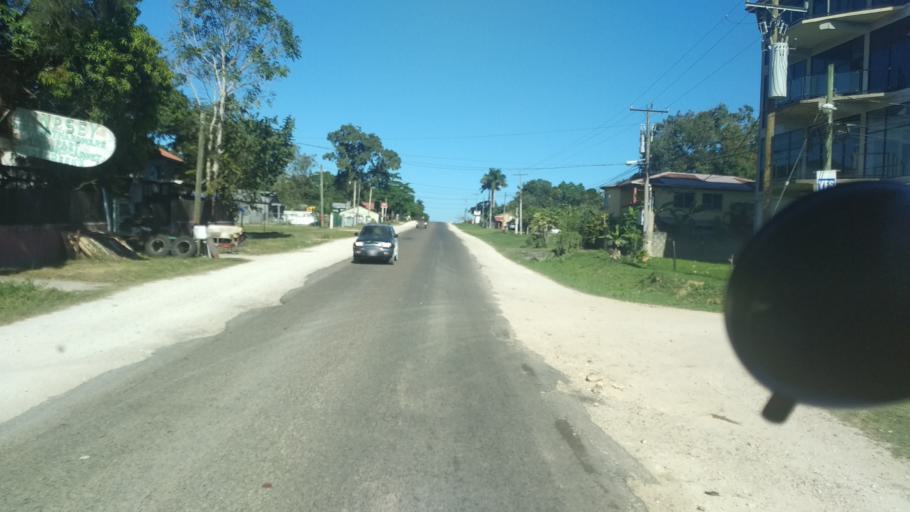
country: BZ
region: Cayo
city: San Ignacio
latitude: 17.1792
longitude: -89.0383
